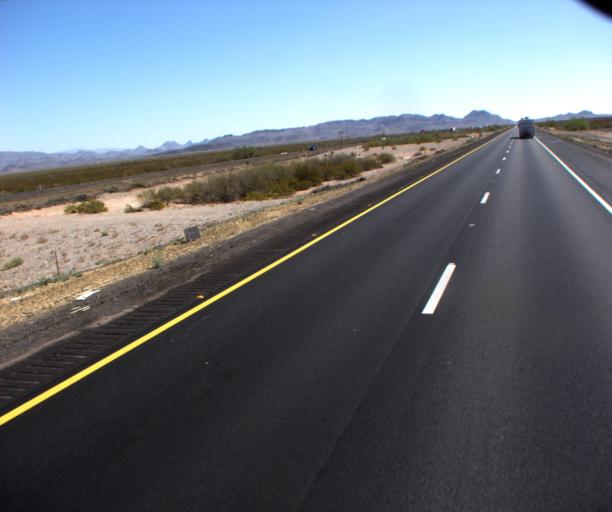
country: US
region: Arizona
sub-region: La Paz County
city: Salome
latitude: 33.6255
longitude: -113.7321
